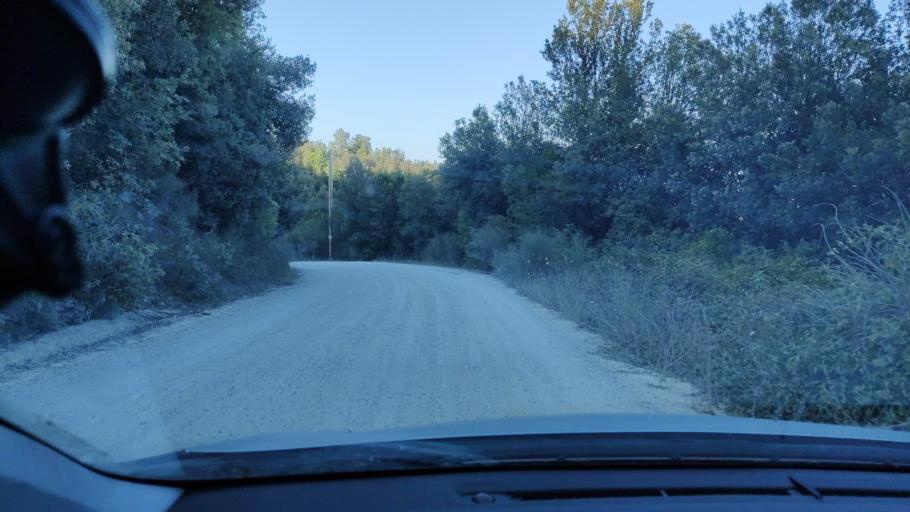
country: IT
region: Umbria
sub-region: Provincia di Terni
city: Amelia
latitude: 42.5372
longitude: 12.3816
